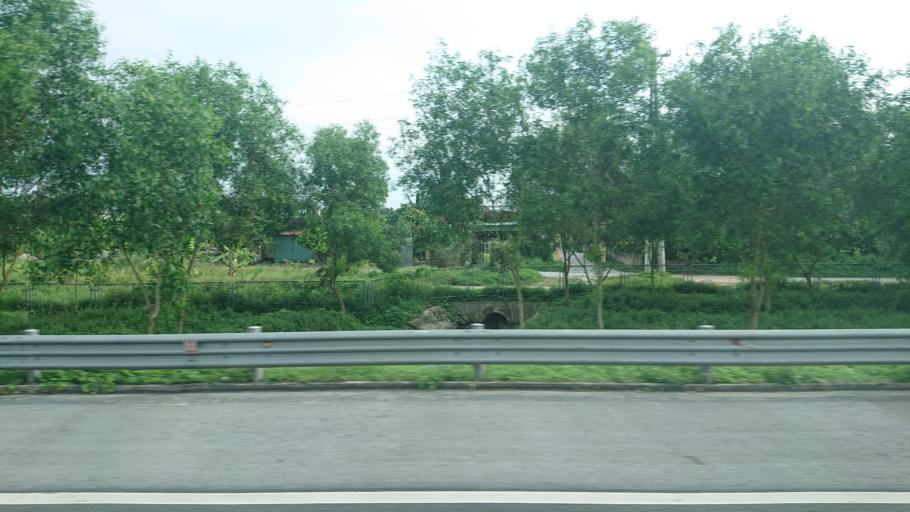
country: VN
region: Hai Phong
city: An Lao
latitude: 20.7885
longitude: 106.5562
